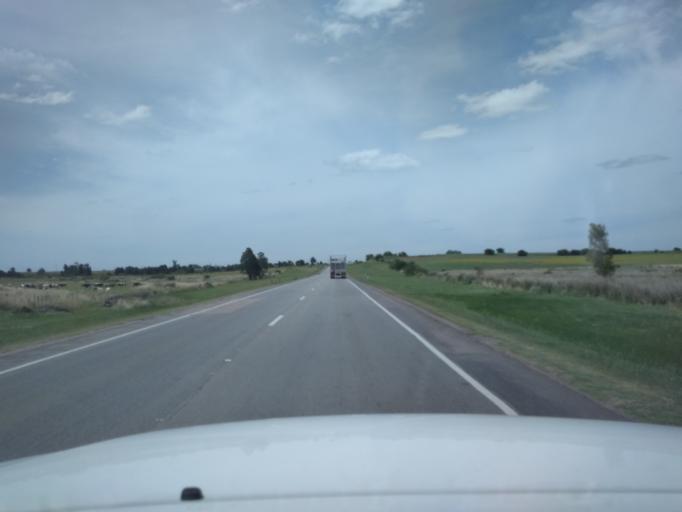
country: UY
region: Florida
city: Cardal
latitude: -34.3269
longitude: -56.2438
